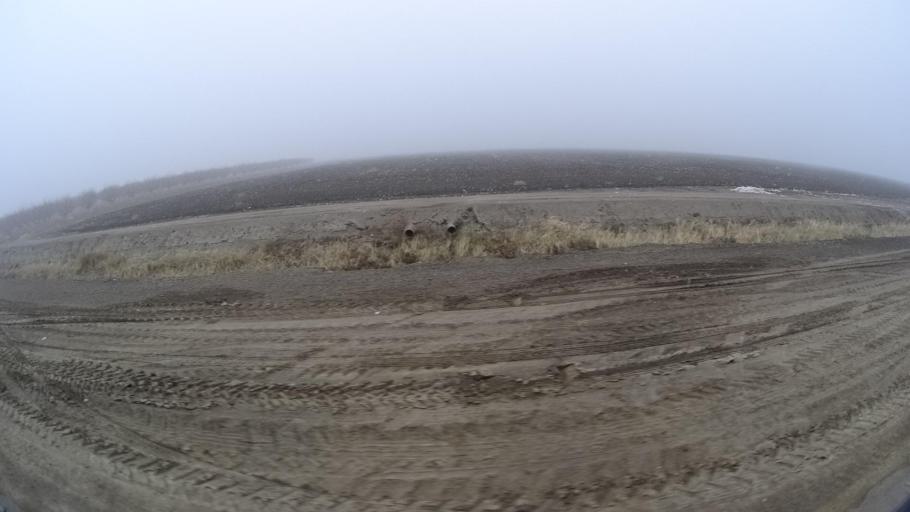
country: US
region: California
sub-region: Kern County
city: Buttonwillow
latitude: 35.4563
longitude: -119.5470
